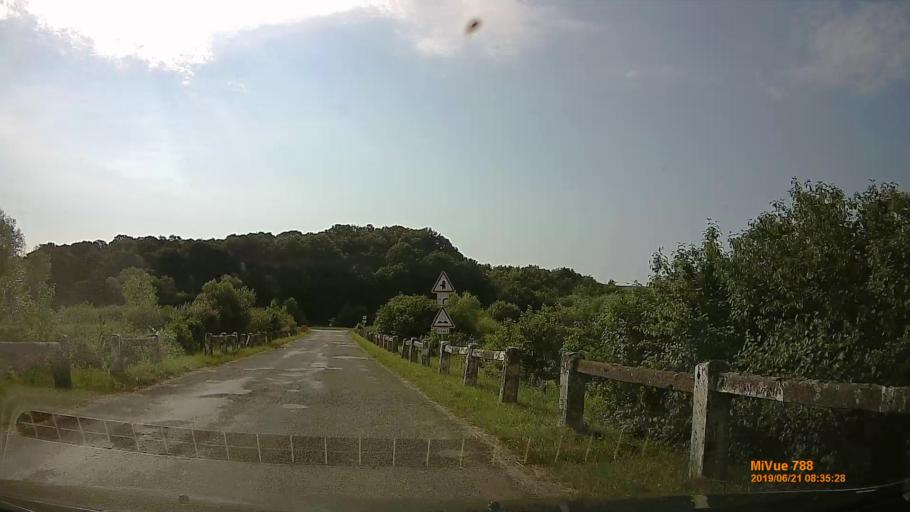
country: HU
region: Baranya
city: Buekkoesd
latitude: 46.1689
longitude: 17.8972
